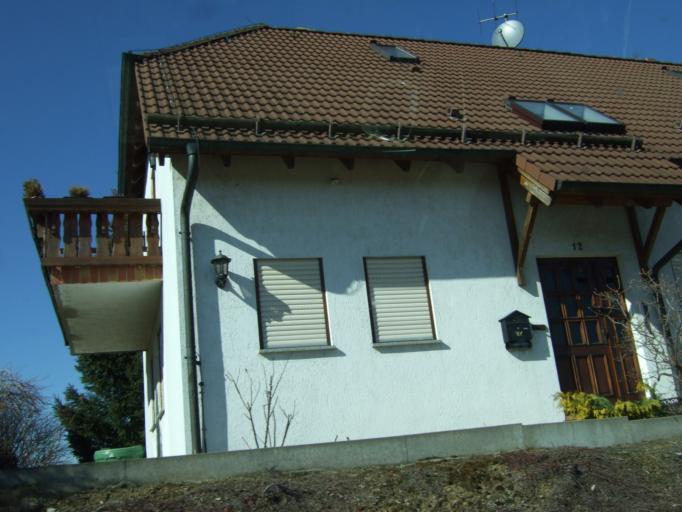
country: DE
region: Saxony
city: Oberschona
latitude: 50.8578
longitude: 13.2414
